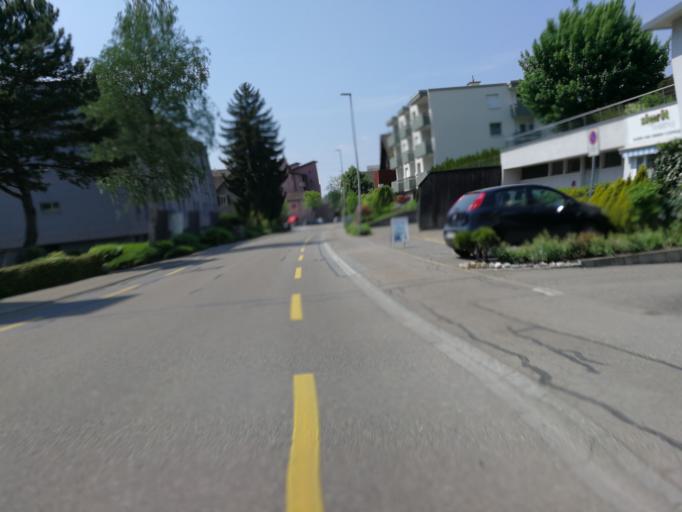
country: CH
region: Saint Gallen
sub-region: Wahlkreis See-Gaster
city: Jona
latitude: 47.2317
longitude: 8.8397
